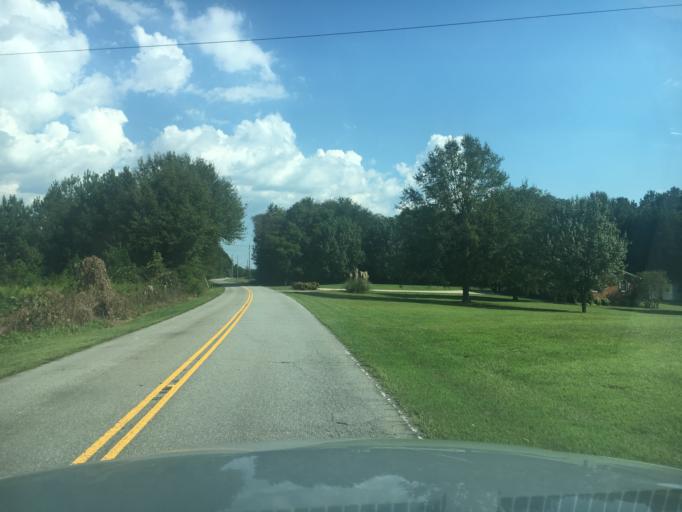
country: US
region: South Carolina
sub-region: Pickens County
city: Liberty
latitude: 34.7460
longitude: -82.6564
